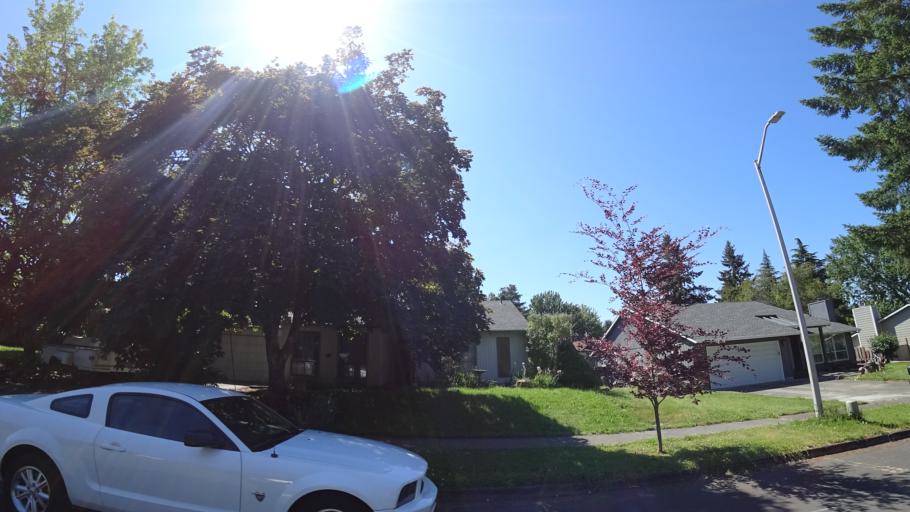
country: US
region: Oregon
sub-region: Washington County
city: Tigard
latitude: 45.4504
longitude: -122.7997
